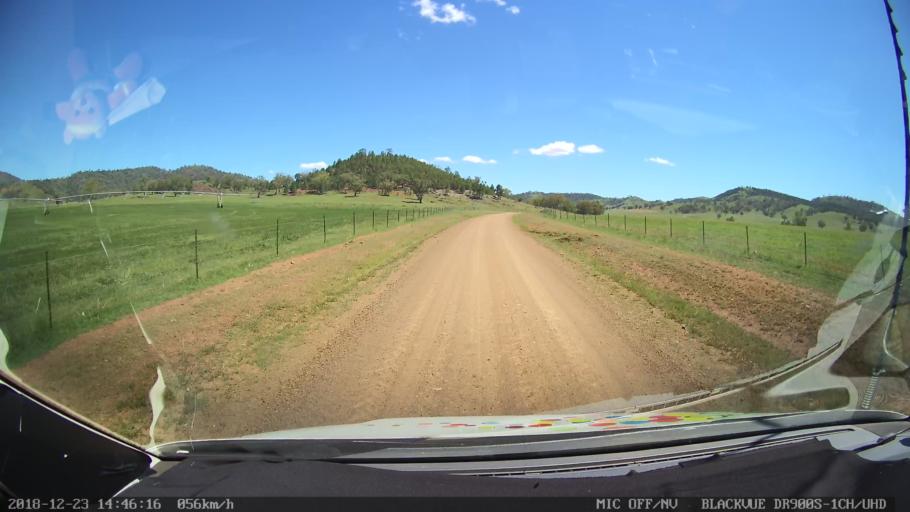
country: AU
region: New South Wales
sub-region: Tamworth Municipality
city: Manilla
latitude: -30.6494
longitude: 150.8795
